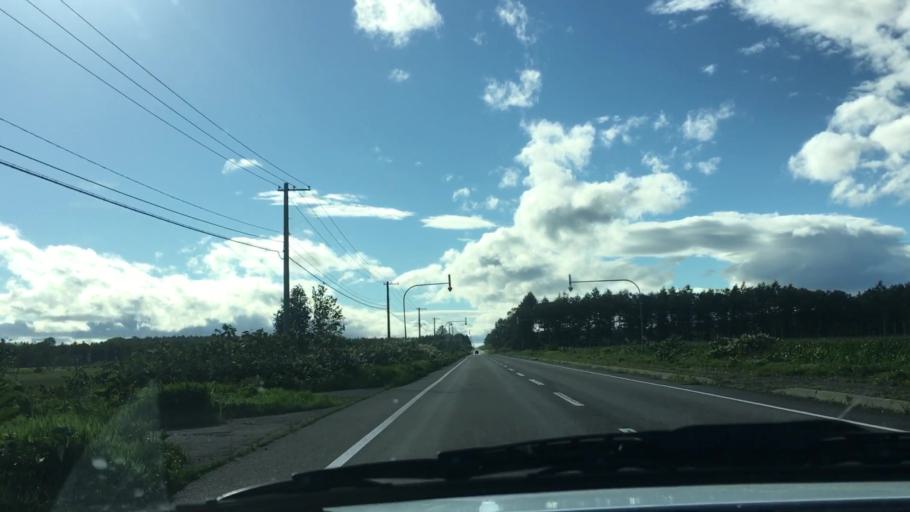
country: JP
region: Hokkaido
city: Otofuke
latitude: 43.1610
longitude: 143.1607
